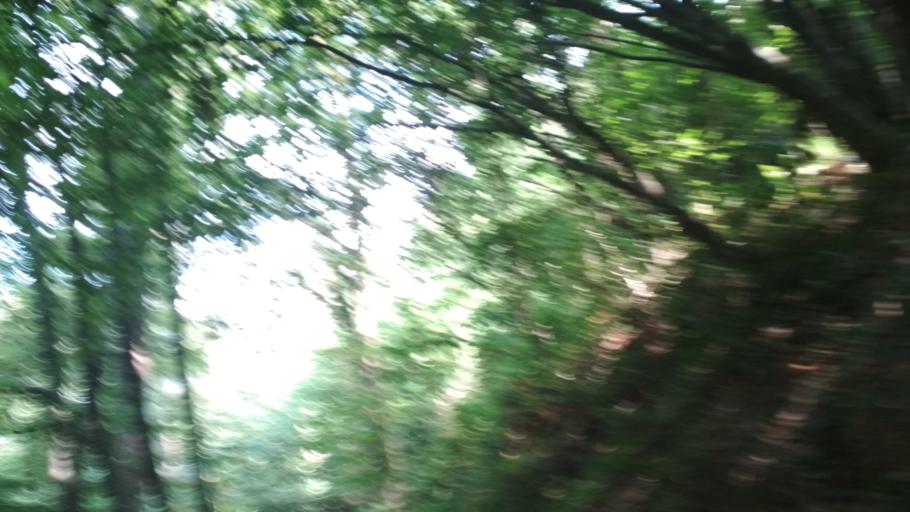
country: ES
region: Basque Country
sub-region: Provincia de Guipuzcoa
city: Hernani
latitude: 43.2896
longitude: -1.9845
